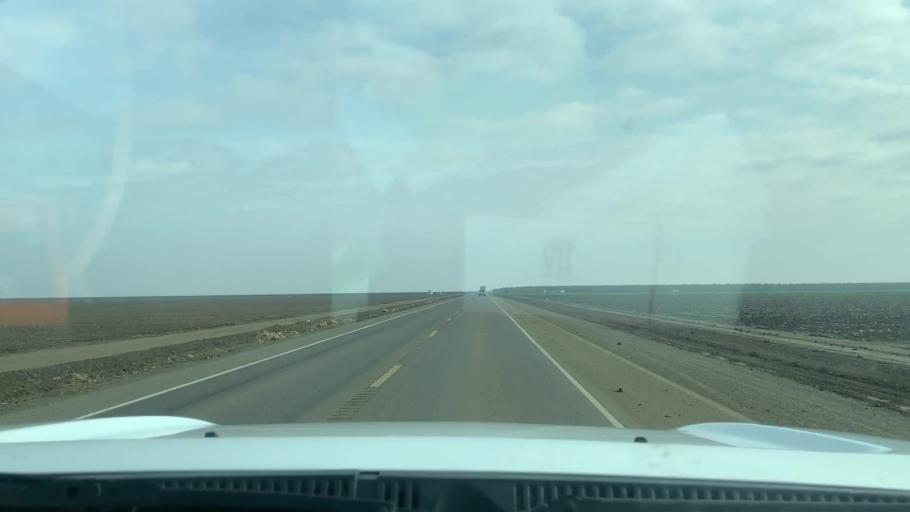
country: US
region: California
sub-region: Fresno County
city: Huron
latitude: 36.2554
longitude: -120.0190
